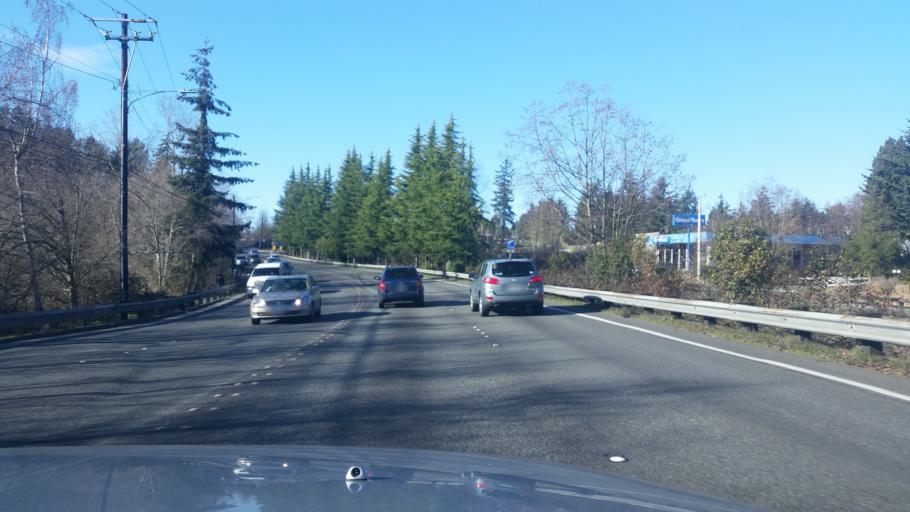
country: US
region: Washington
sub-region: Snohomish County
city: Lynnwood
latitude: 47.8215
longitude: -122.3057
